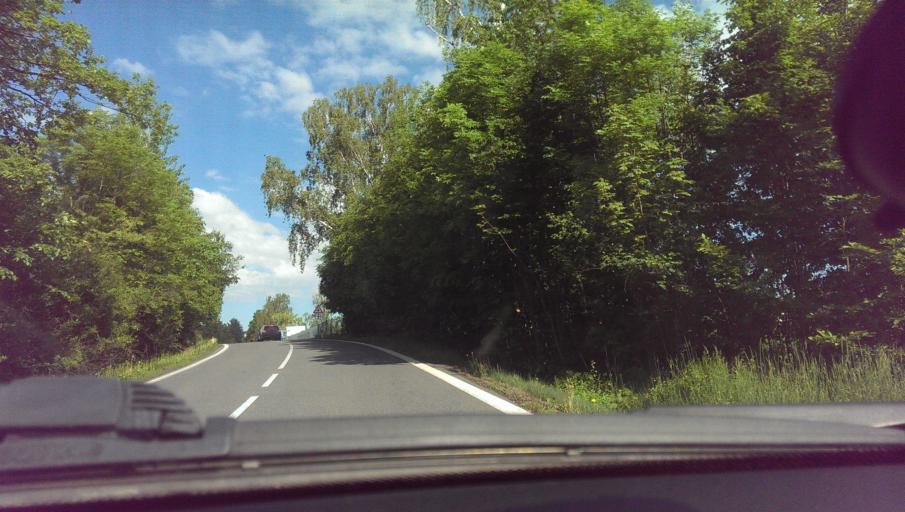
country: CZ
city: Kuncice pod Ondrejnikem
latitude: 49.5466
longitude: 18.2582
